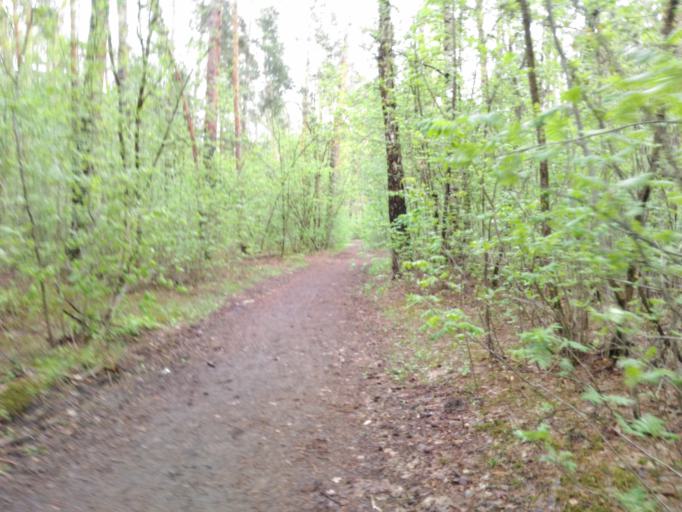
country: RU
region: Moscow
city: Strogino
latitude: 55.7806
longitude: 37.4144
